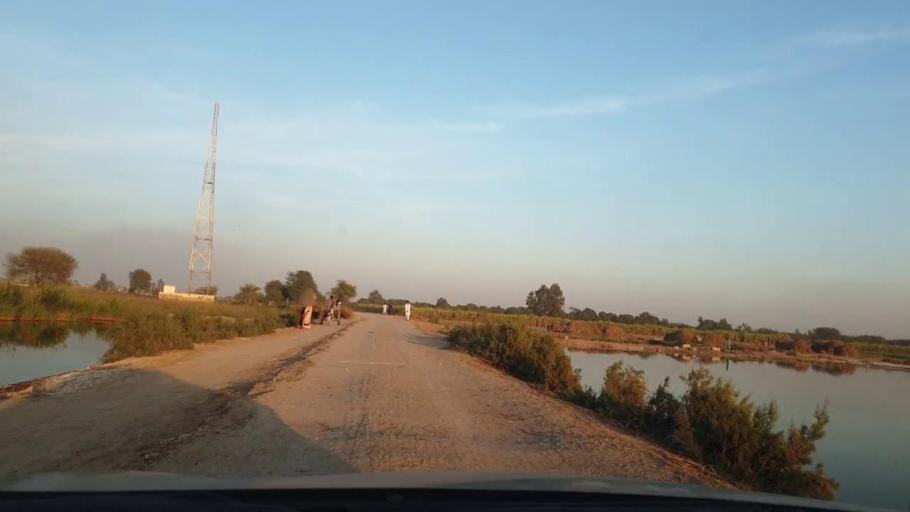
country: PK
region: Sindh
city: Tando Allahyar
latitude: 25.6096
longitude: 68.6876
